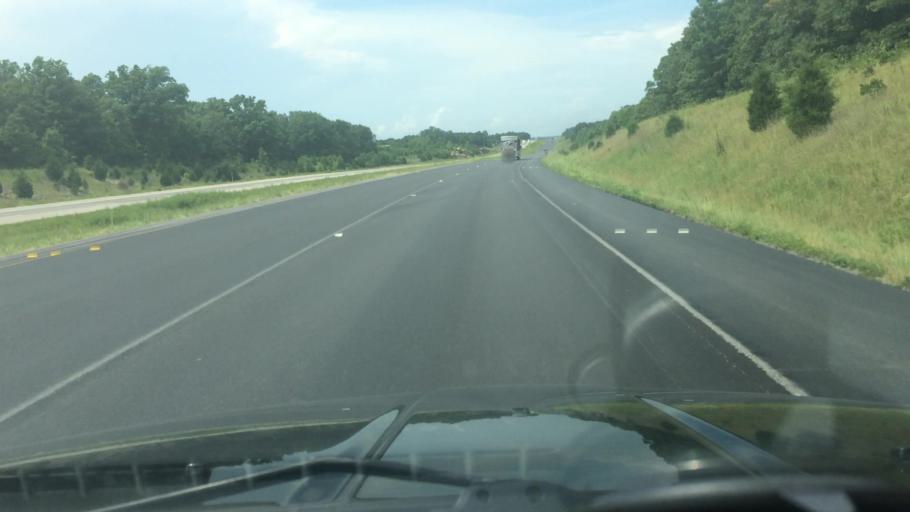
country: US
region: Missouri
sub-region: Saint Clair County
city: Osceola
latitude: 37.9541
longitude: -93.6413
